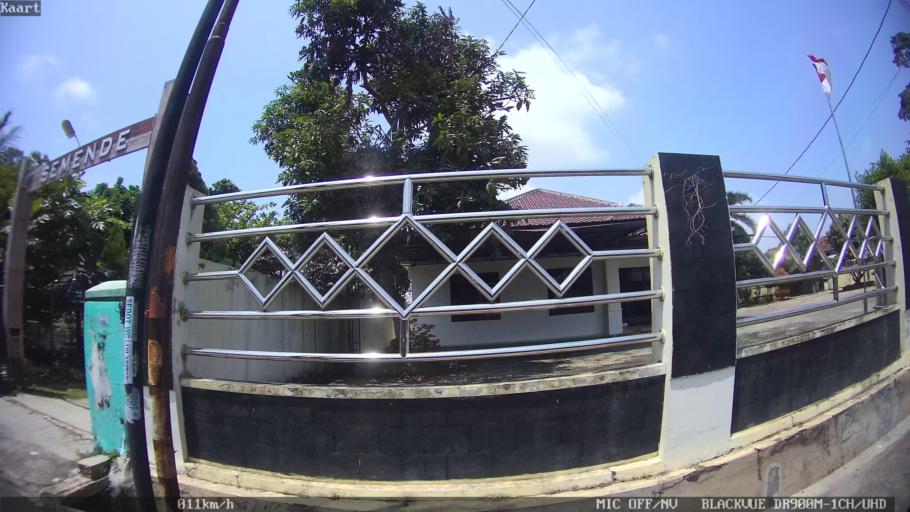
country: ID
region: Lampung
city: Kedaton
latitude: -5.3736
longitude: 105.2682
